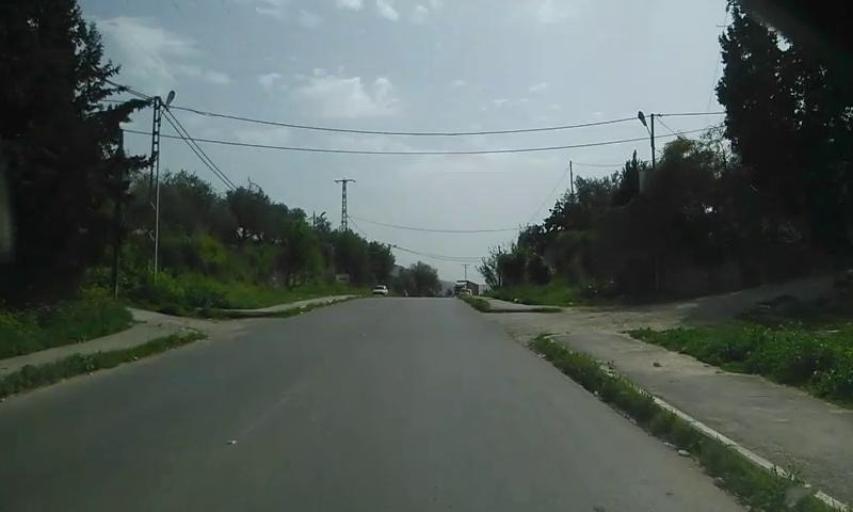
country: PS
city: Bir al Basha
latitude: 32.4199
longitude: 35.2307
